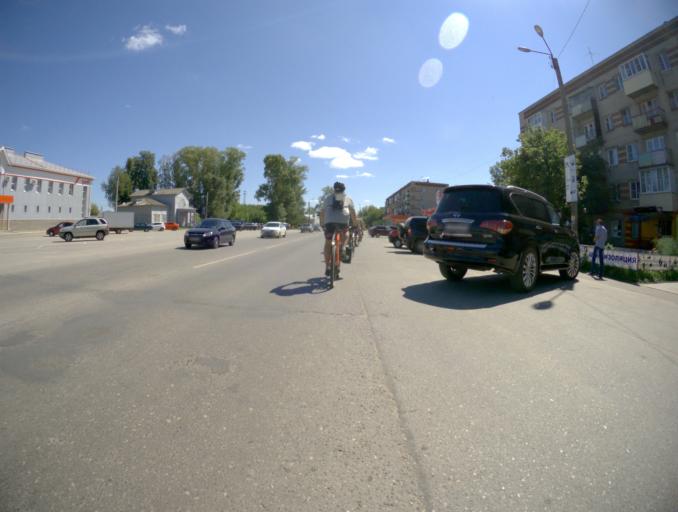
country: RU
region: Nizjnij Novgorod
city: Bor
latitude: 56.3578
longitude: 44.0712
